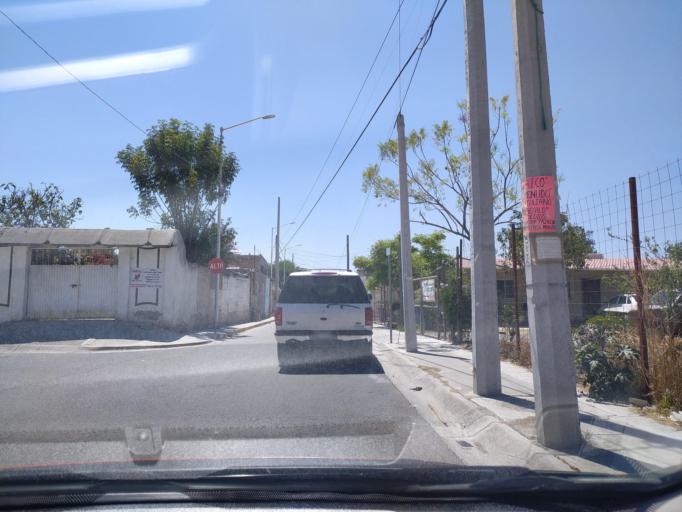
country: MX
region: Guanajuato
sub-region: San Francisco del Rincon
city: Estacion de San Francisco
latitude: 21.0264
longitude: -101.8298
